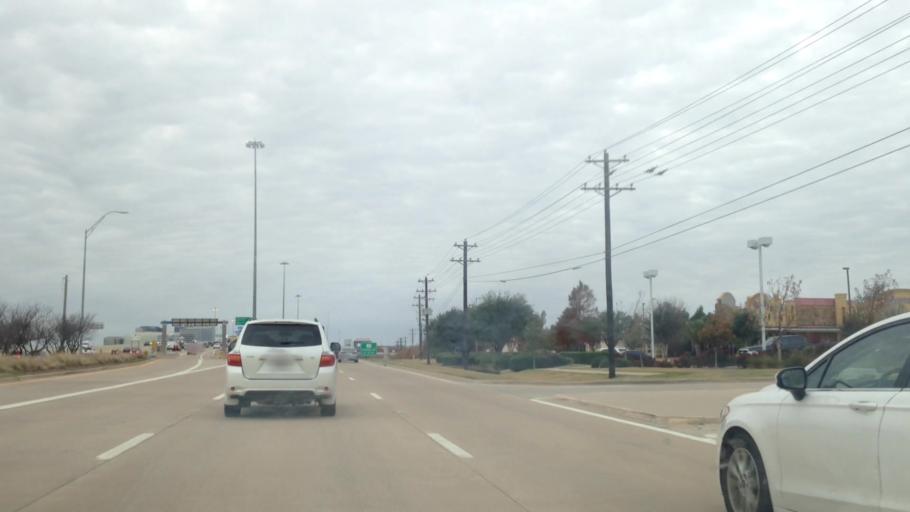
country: US
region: Texas
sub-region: Collin County
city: Frisco
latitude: 33.1003
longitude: -96.7993
